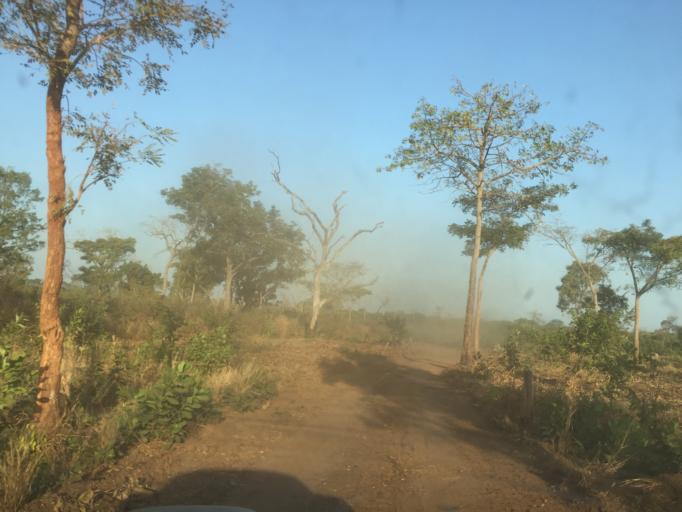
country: GW
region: Oio
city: Farim
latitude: 12.5291
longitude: -15.2771
